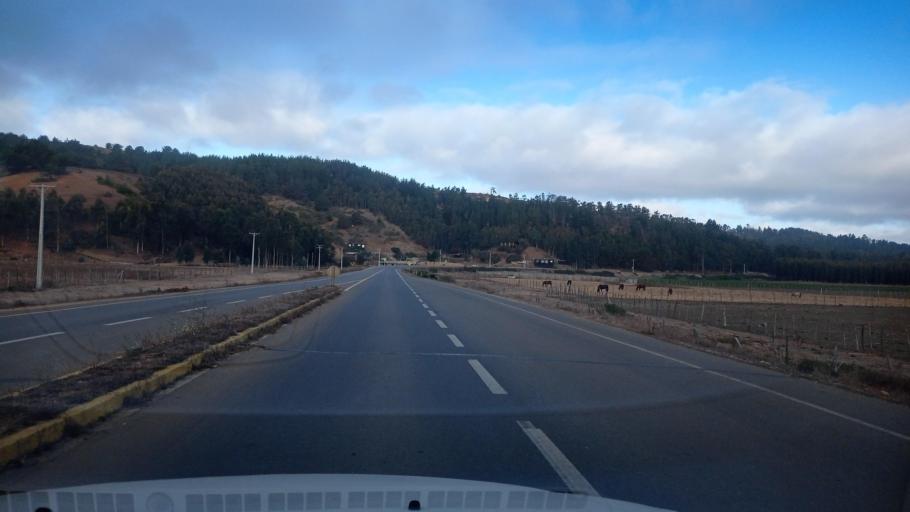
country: CL
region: O'Higgins
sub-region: Provincia de Colchagua
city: Santa Cruz
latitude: -34.4660
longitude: -72.0222
